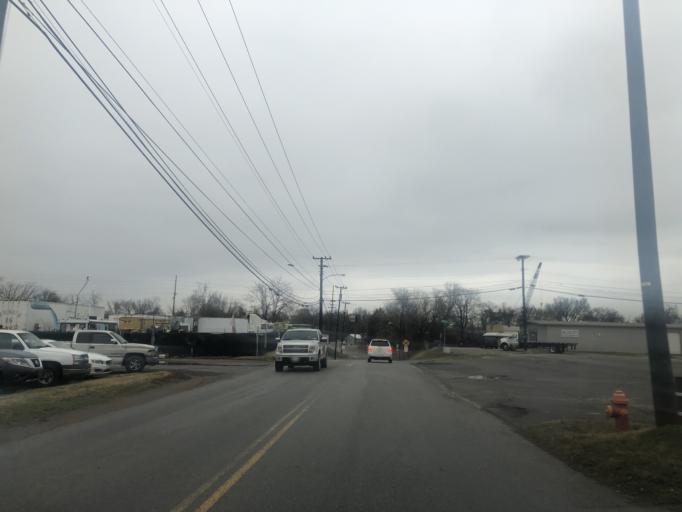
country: US
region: Tennessee
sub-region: Davidson County
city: Nashville
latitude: 36.1417
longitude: -86.7313
